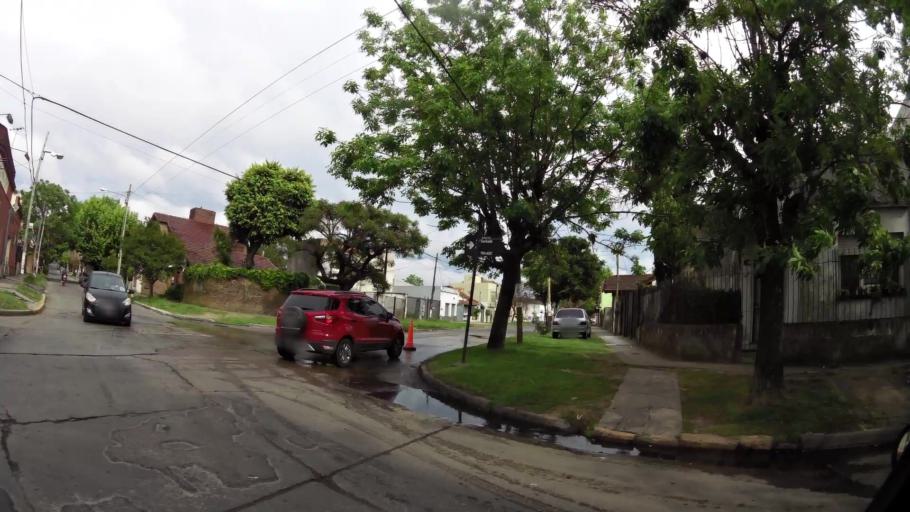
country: AR
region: Buenos Aires
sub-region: Partido de Quilmes
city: Quilmes
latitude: -34.7182
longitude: -58.2458
